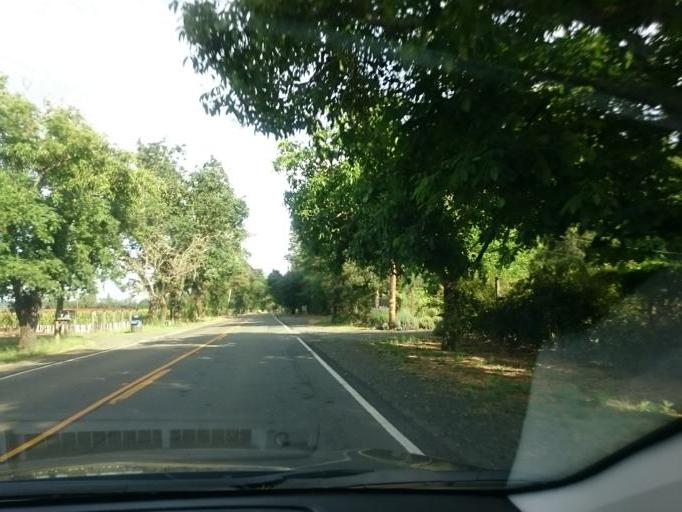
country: US
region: California
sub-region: Napa County
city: Calistoga
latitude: 38.5928
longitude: -122.6123
